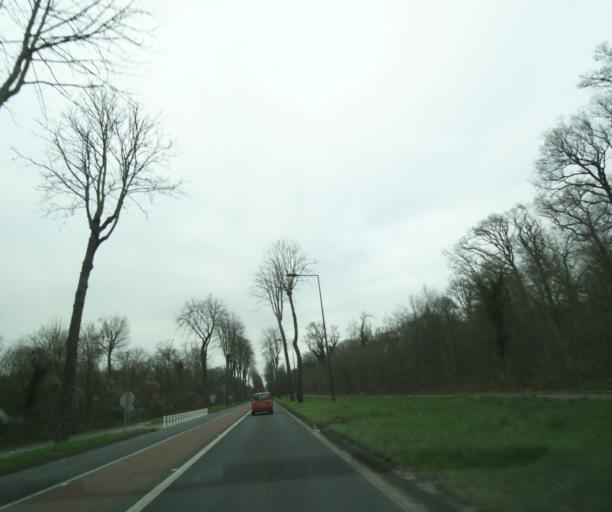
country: FR
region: Ile-de-France
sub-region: Departement des Yvelines
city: Poissy
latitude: 48.9162
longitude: 2.0653
